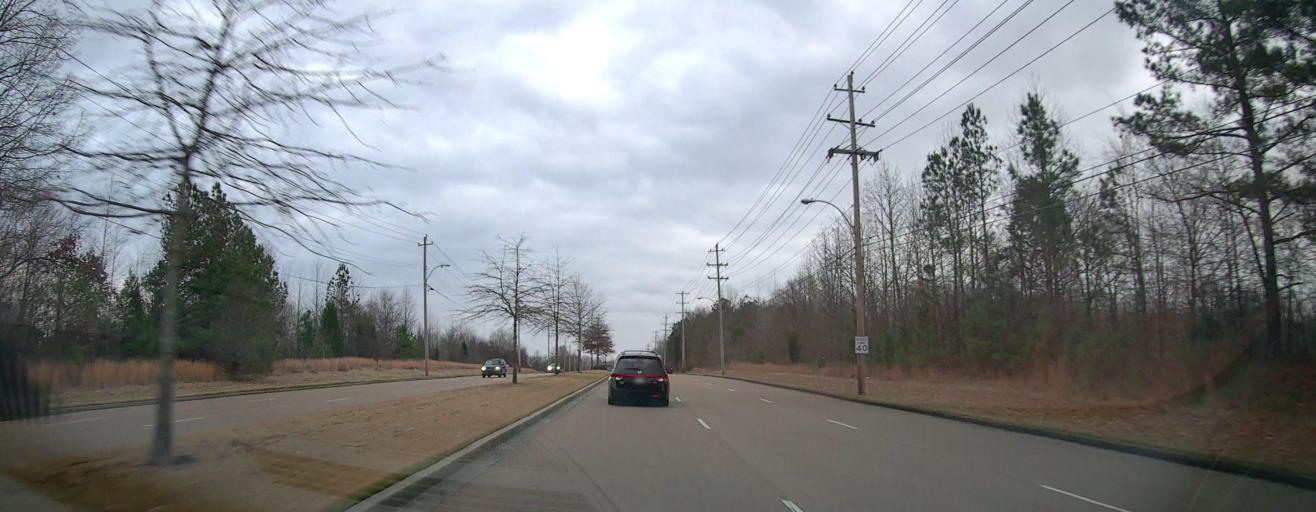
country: US
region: Tennessee
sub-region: Shelby County
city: Collierville
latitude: 35.0471
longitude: -89.7398
